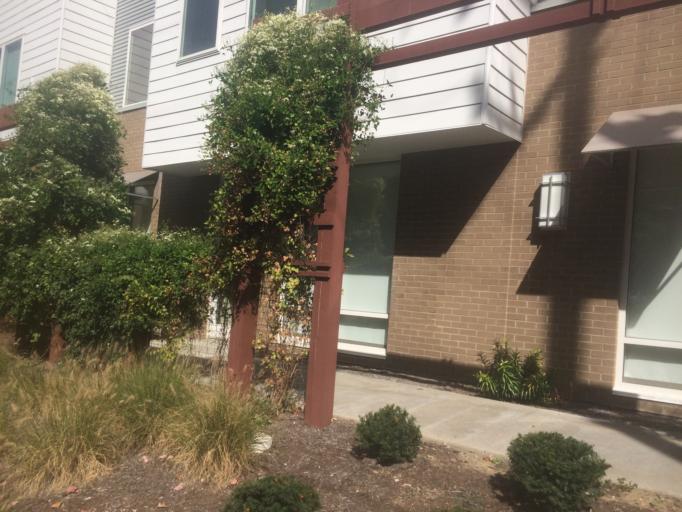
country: US
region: Ohio
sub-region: Cuyahoga County
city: East Cleveland
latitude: 41.5110
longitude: -81.6040
